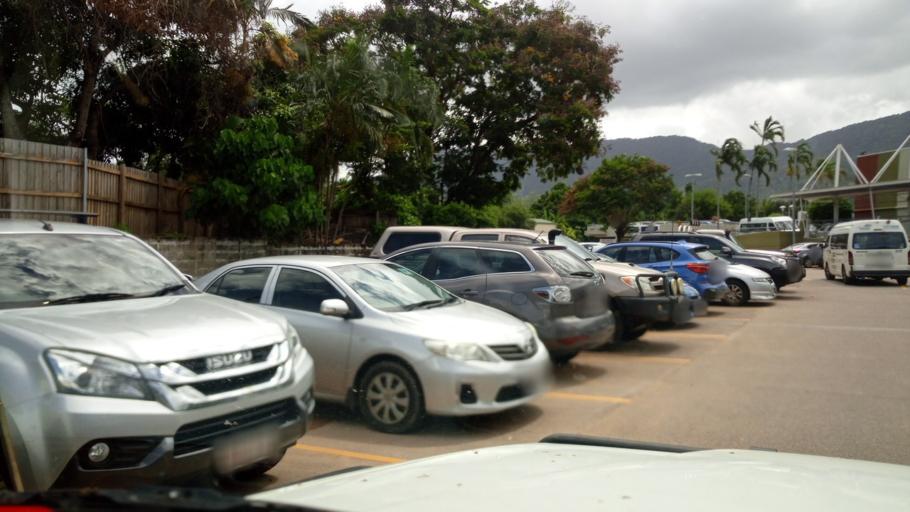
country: AU
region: Queensland
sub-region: Cairns
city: Woree
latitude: -16.9452
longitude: 145.7407
